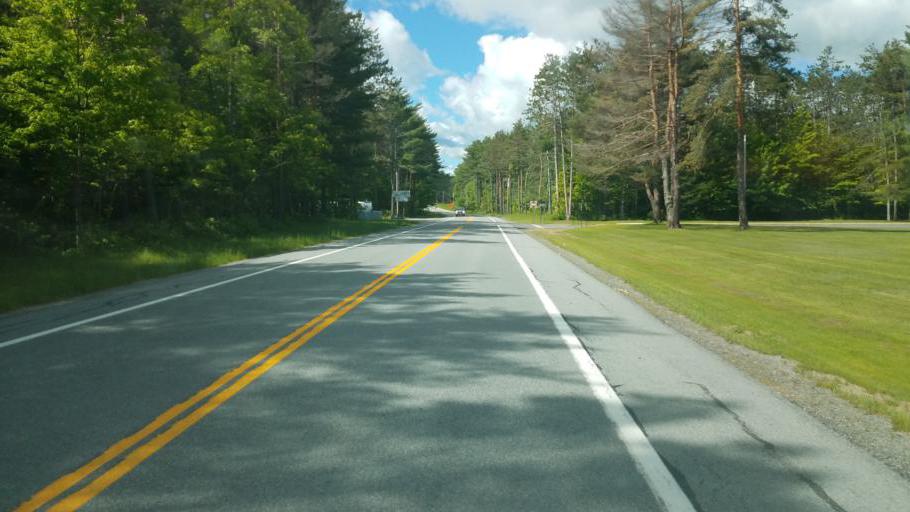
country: US
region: New York
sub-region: Oneida County
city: Boonville
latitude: 43.4323
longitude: -75.2127
